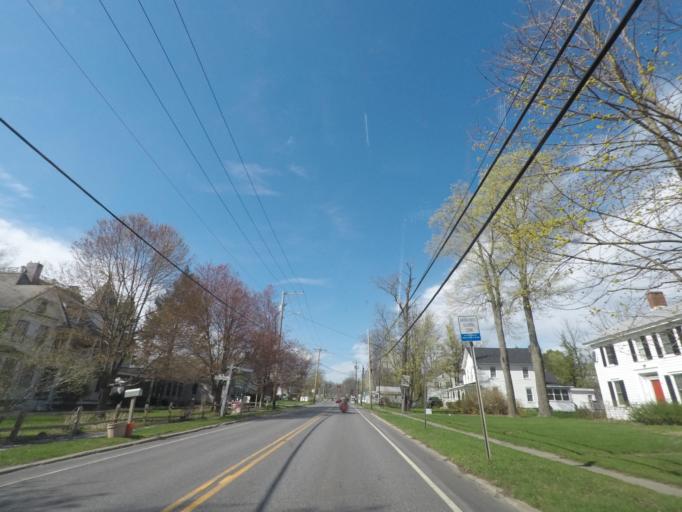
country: US
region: New York
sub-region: Greene County
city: Cairo
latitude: 42.4141
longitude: -74.0219
